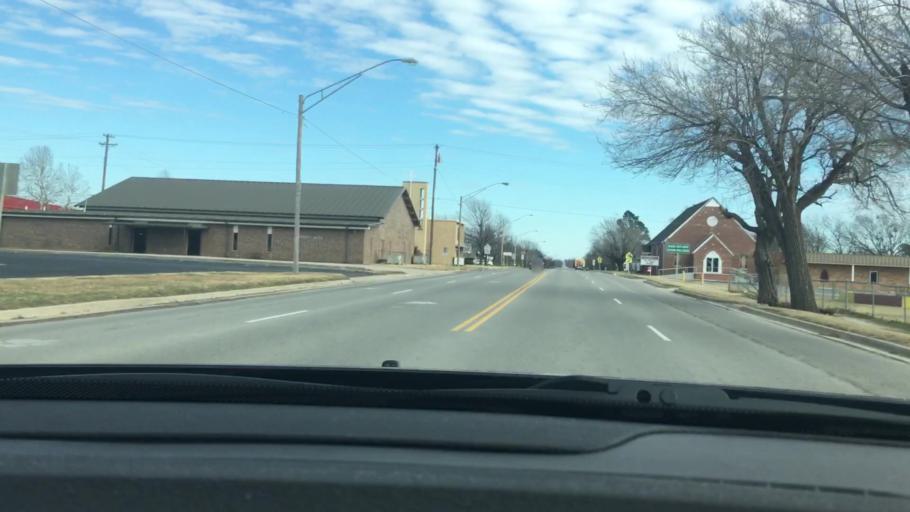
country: US
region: Oklahoma
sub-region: Garvin County
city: Stratford
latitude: 34.7966
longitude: -96.9611
